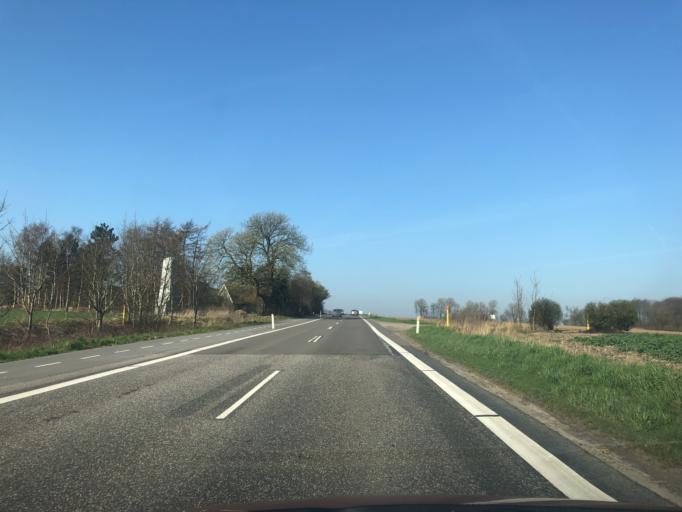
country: DK
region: Zealand
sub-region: Faxe Kommune
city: Fakse
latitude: 55.2553
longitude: 12.0930
